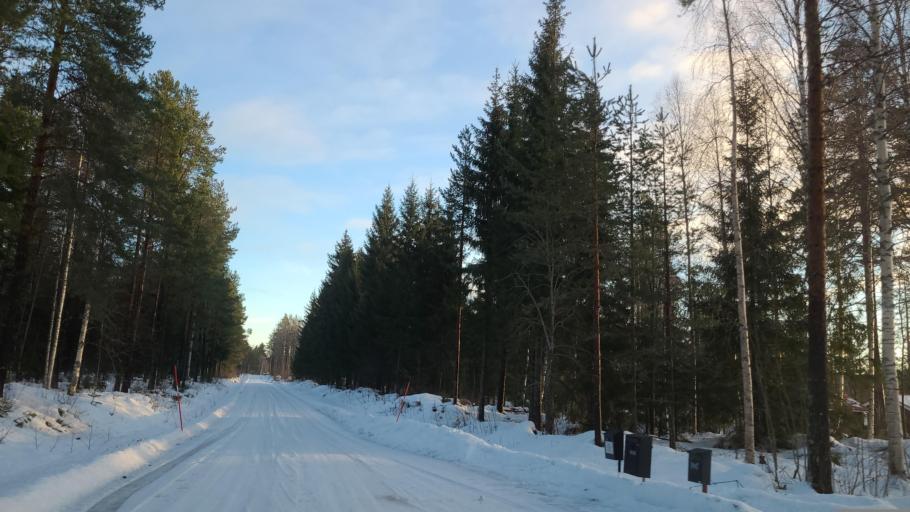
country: SE
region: Gaevleborg
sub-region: Bollnas Kommun
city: Kilafors
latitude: 61.4002
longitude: 16.6495
